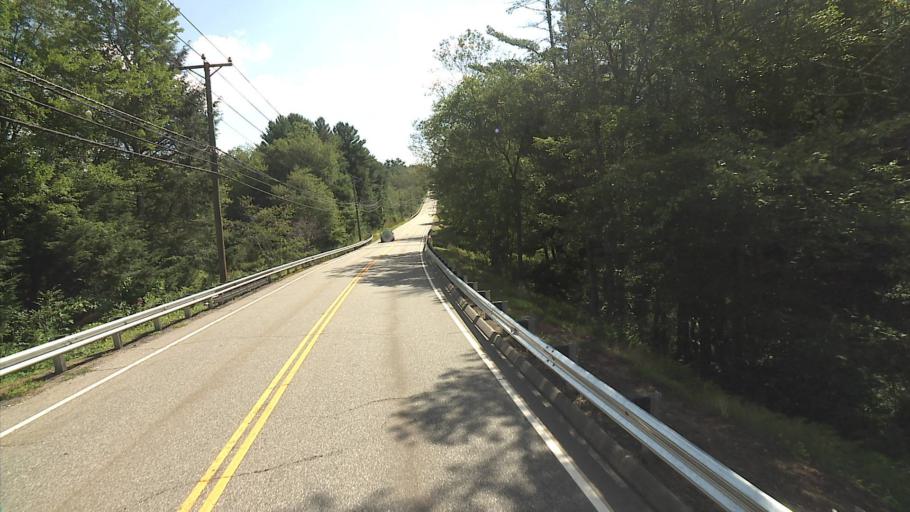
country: US
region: Connecticut
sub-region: Tolland County
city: Stafford
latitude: 41.9632
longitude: -72.2480
